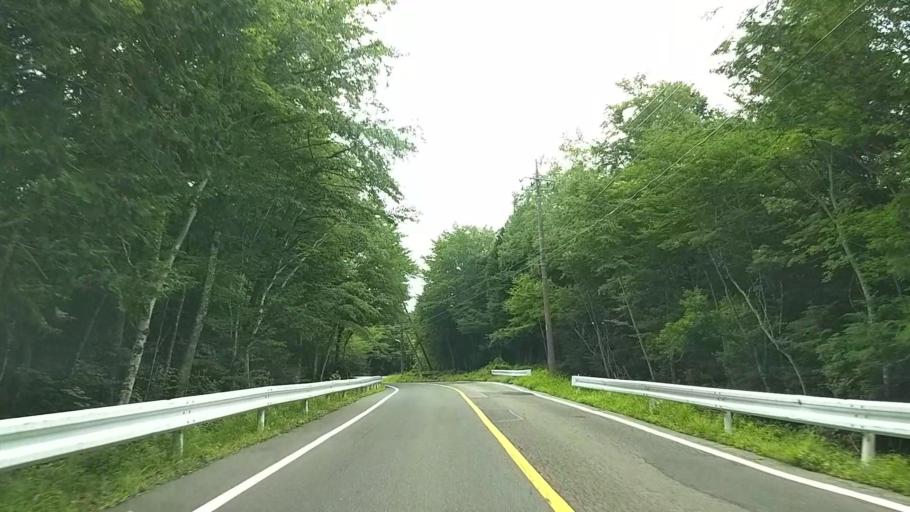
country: JP
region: Yamanashi
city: Fujikawaguchiko
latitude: 35.4888
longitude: 138.6688
